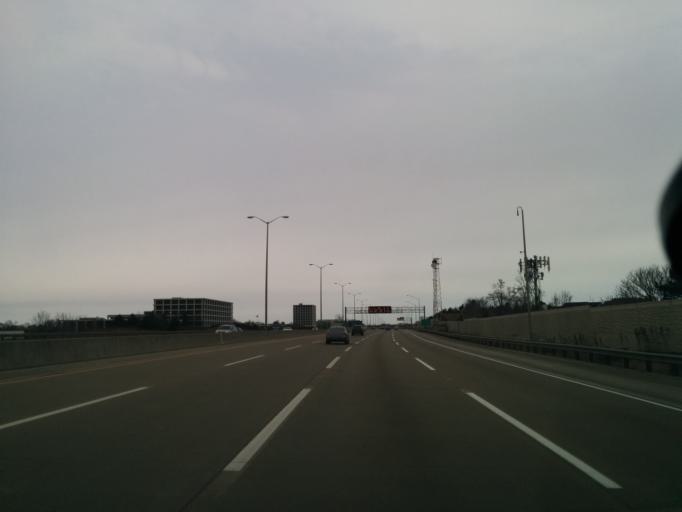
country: US
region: Illinois
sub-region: Cook County
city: Northbrook
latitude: 42.0921
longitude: -87.8680
